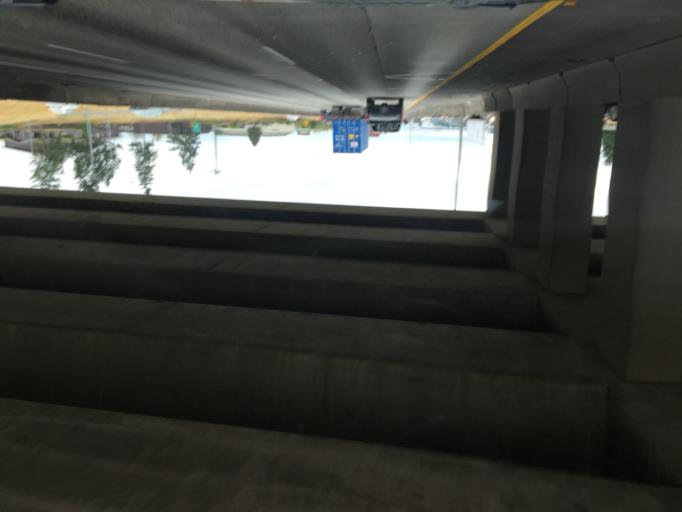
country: US
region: Washington
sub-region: Pierce County
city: Tacoma
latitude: 47.2231
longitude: -122.4635
